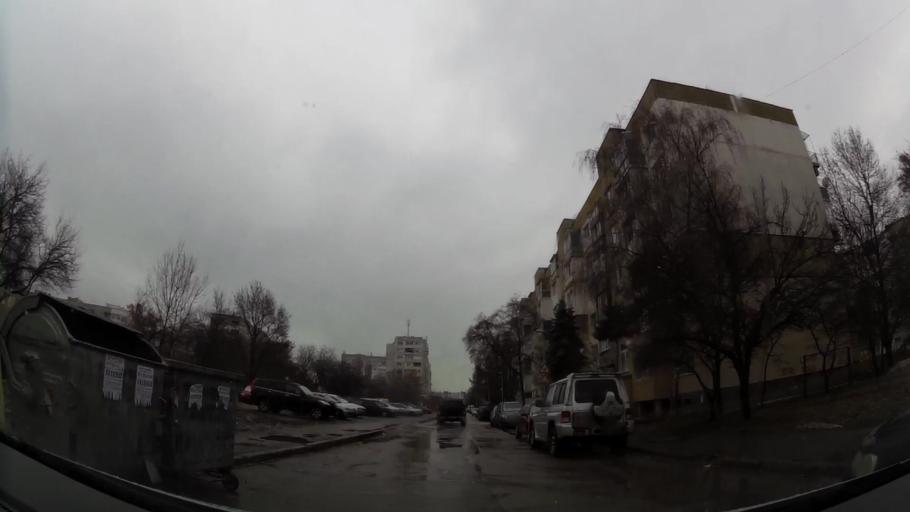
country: BG
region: Sofia-Capital
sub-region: Stolichna Obshtina
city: Sofia
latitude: 42.6681
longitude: 23.3875
